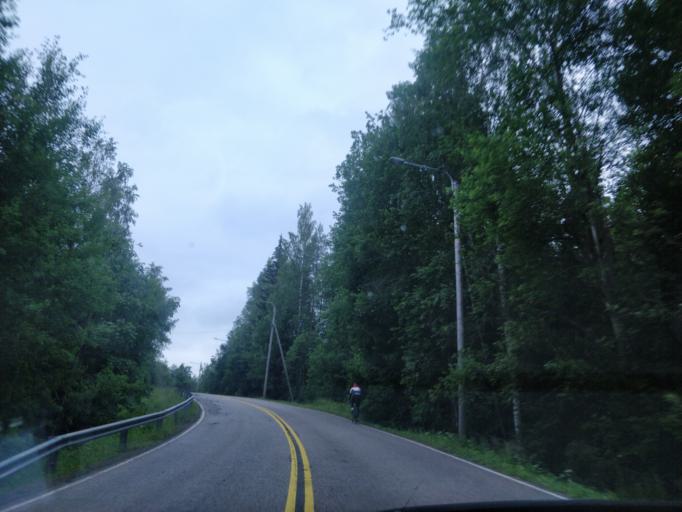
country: FI
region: Uusimaa
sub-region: Helsinki
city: Kauniainen
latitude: 60.3020
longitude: 24.6978
